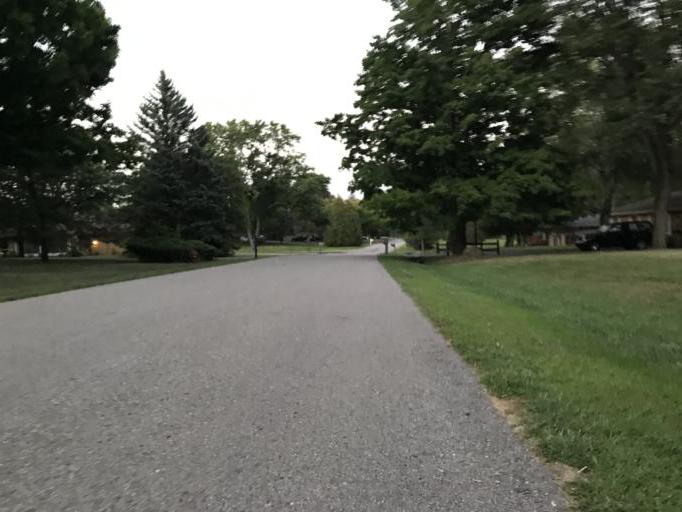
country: US
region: Michigan
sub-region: Oakland County
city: Farmington Hills
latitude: 42.4859
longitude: -83.3561
